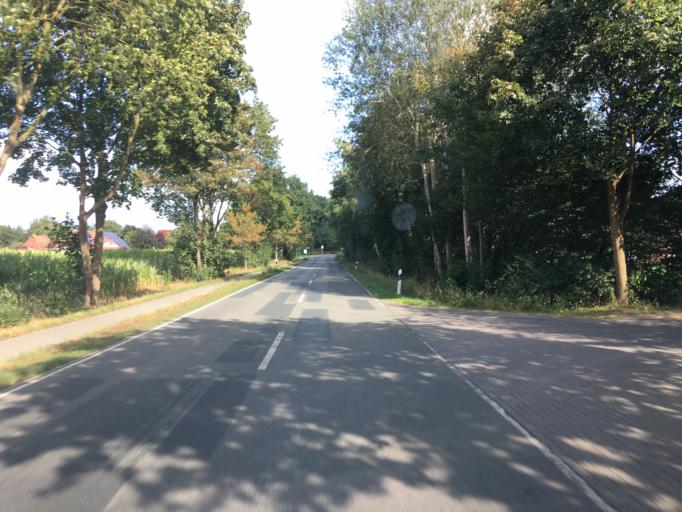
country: DE
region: Lower Saxony
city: Wardenburg
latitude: 53.0673
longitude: 8.1836
